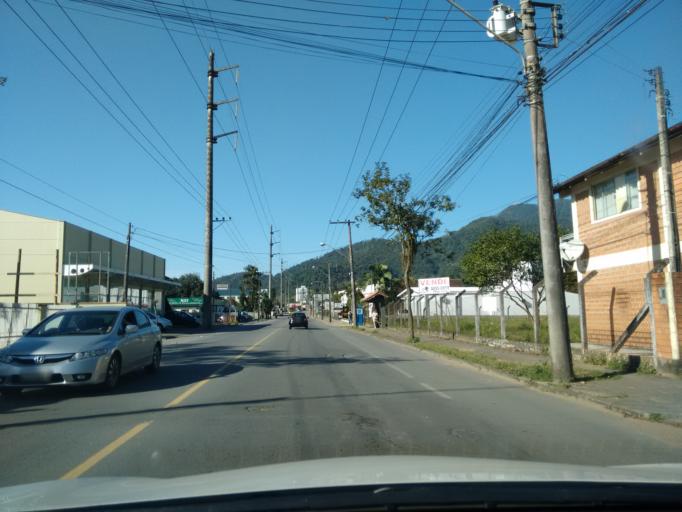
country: BR
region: Santa Catarina
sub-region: Jaragua Do Sul
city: Jaragua do Sul
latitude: -26.5071
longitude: -49.0981
